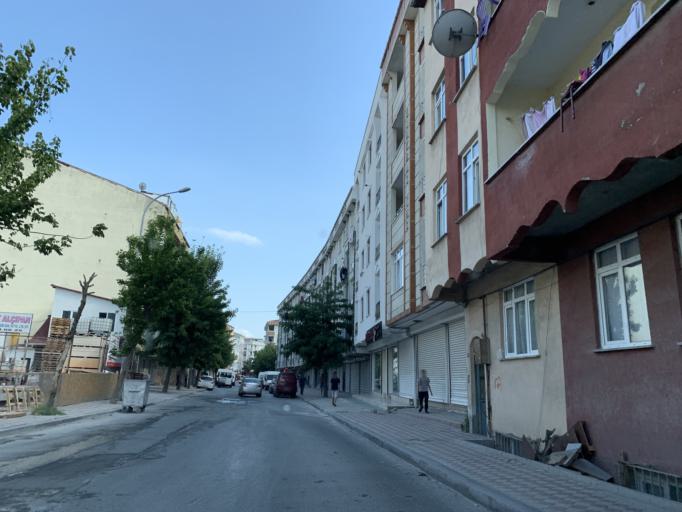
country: TR
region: Istanbul
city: Esenyurt
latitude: 41.0398
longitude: 28.6741
